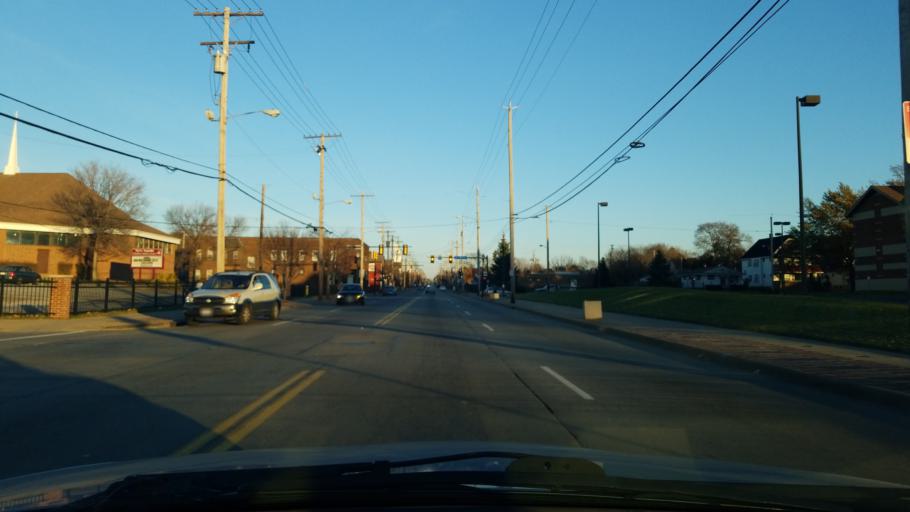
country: US
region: Ohio
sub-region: Cuyahoga County
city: Shaker Heights
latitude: 41.4644
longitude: -81.5801
